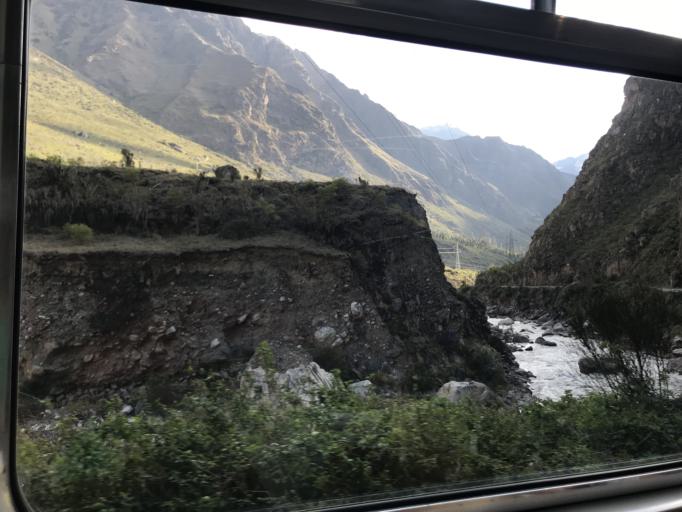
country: PE
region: Cusco
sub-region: Provincia de Urubamba
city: Ollantaytambo
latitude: -13.2211
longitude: -72.3937
